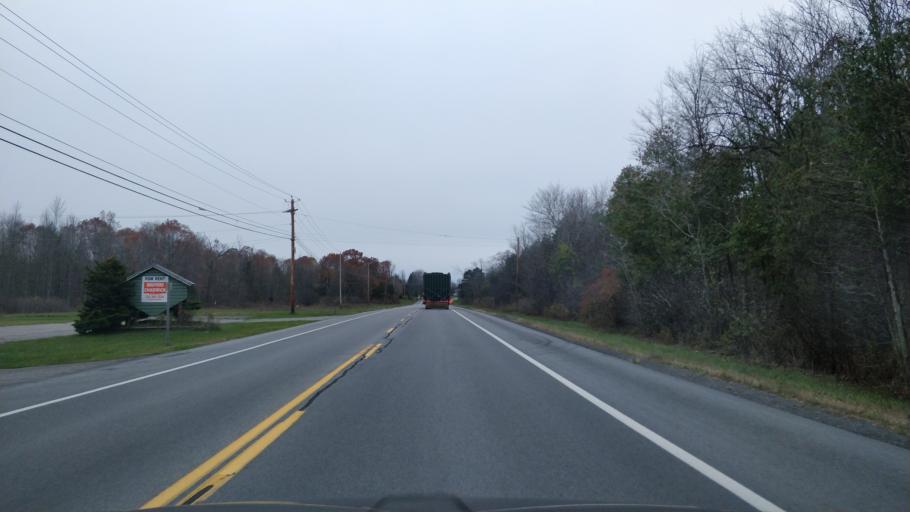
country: CA
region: Ontario
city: Brockville
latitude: 44.5993
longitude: -75.6270
